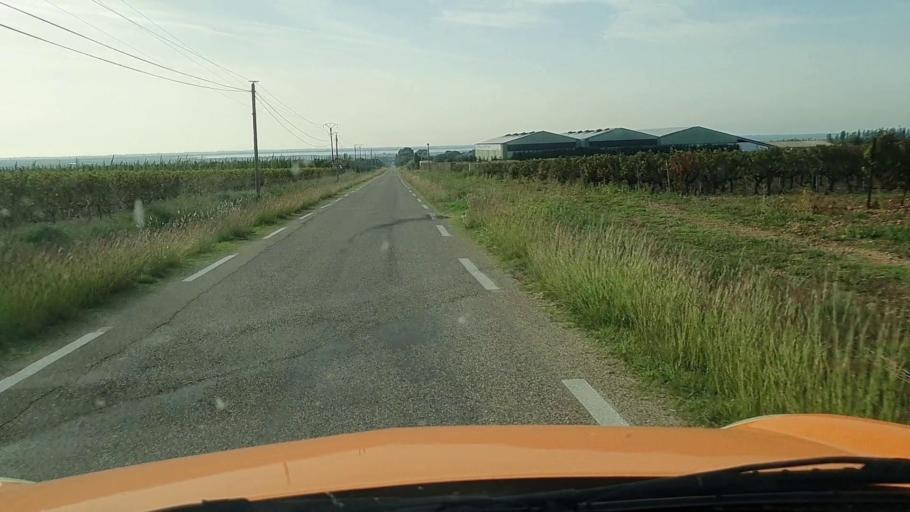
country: FR
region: Languedoc-Roussillon
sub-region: Departement du Gard
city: Beauvoisin
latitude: 43.6649
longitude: 4.3422
